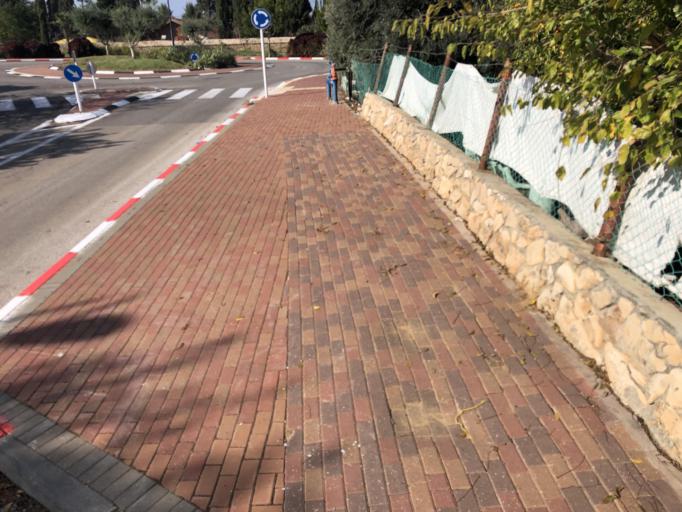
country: IL
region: Northern District
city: `Akko
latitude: 32.9401
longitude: 35.0934
